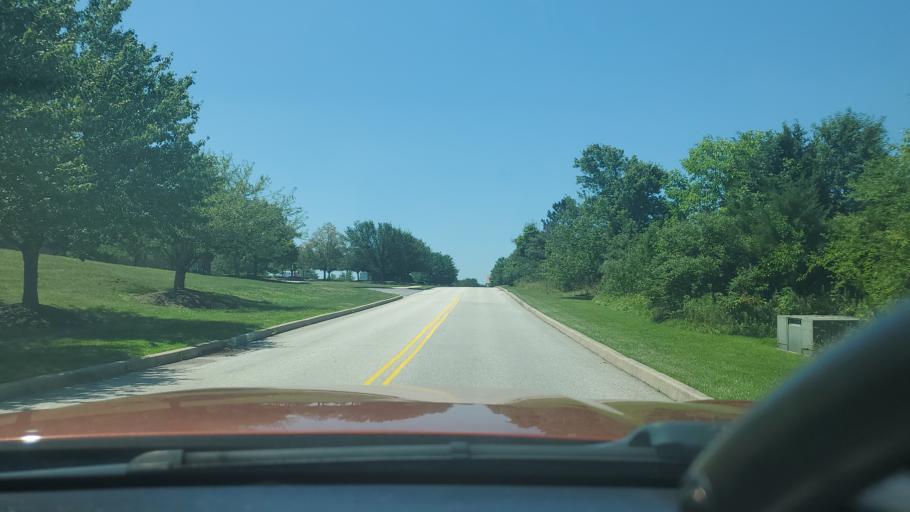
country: US
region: Pennsylvania
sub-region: Montgomery County
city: Limerick
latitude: 40.2240
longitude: -75.5549
